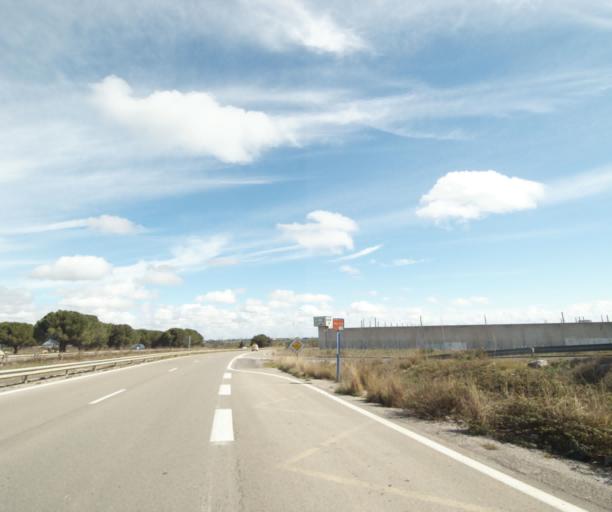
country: FR
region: Languedoc-Roussillon
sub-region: Departement de l'Herault
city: Saint-Jean-de-Vedas
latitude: 43.5456
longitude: 3.8238
